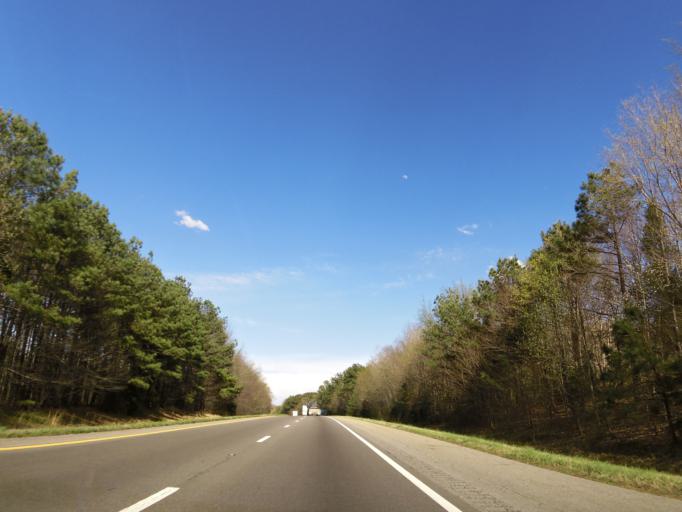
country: US
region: Tennessee
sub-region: Dickson County
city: Dickson
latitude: 36.0085
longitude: -87.3905
